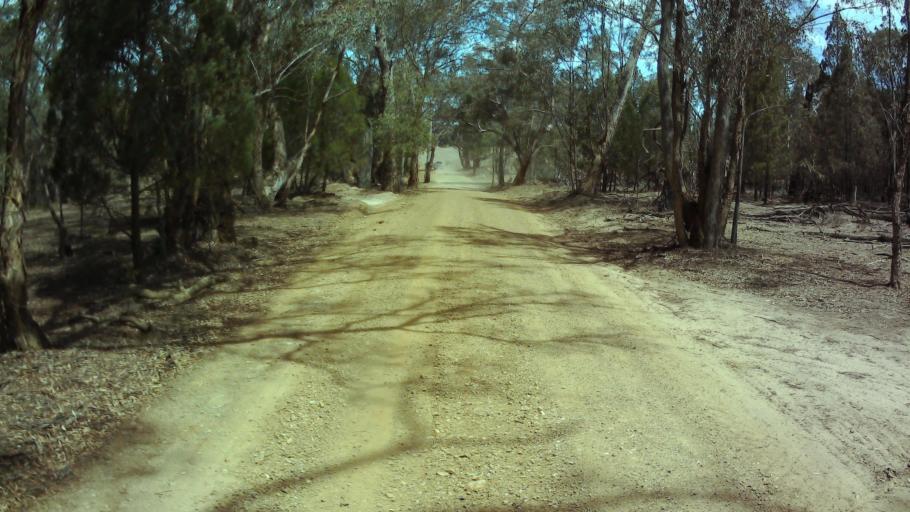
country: AU
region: New South Wales
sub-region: Weddin
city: Grenfell
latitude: -33.8192
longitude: 148.1669
